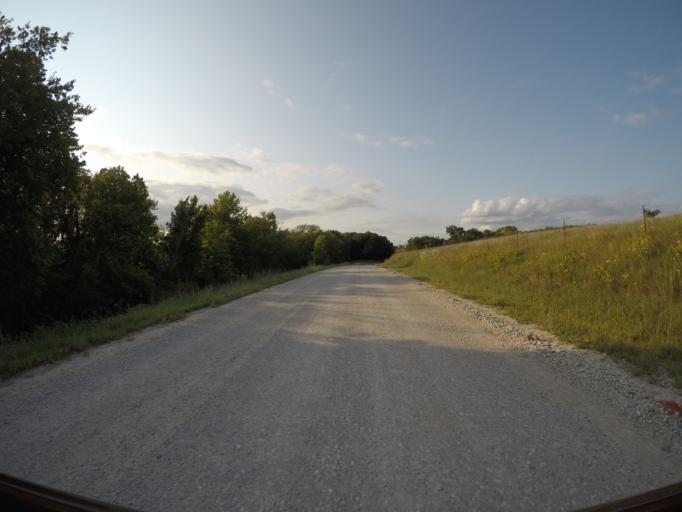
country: US
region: Kansas
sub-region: Wabaunsee County
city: Alma
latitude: 38.9695
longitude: -96.2623
